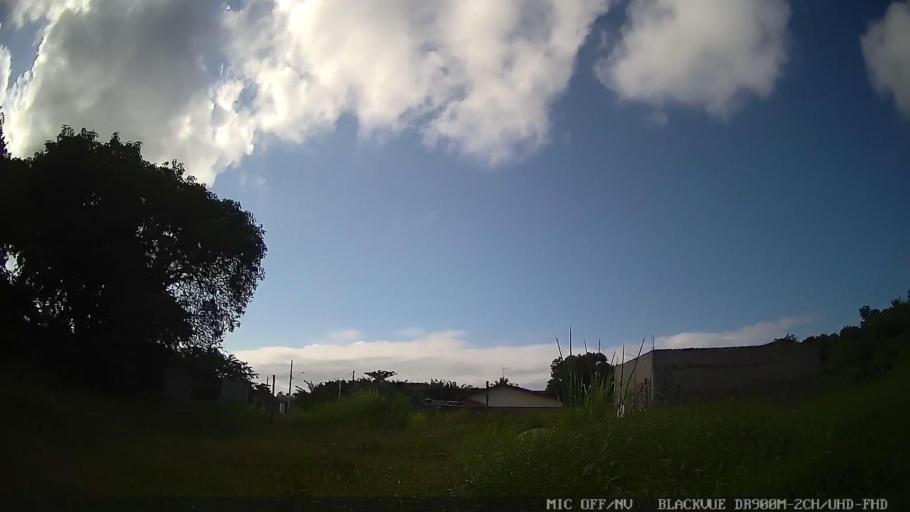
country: BR
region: Sao Paulo
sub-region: Peruibe
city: Peruibe
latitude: -24.2703
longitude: -46.9438
